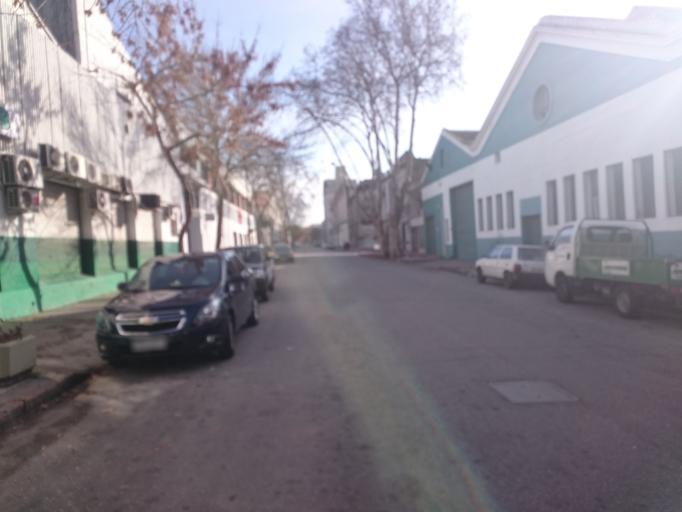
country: UY
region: Montevideo
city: Montevideo
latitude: -34.8975
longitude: -56.1911
